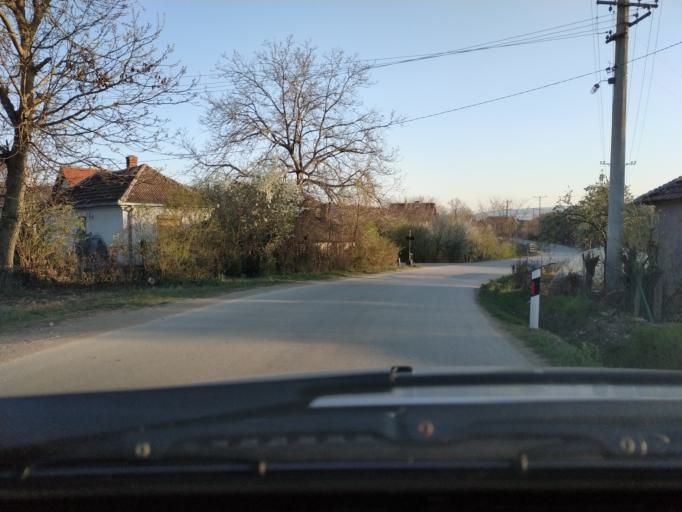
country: RS
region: Central Serbia
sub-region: Nisavski Okrug
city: Aleksinac
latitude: 43.4961
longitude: 21.7858
